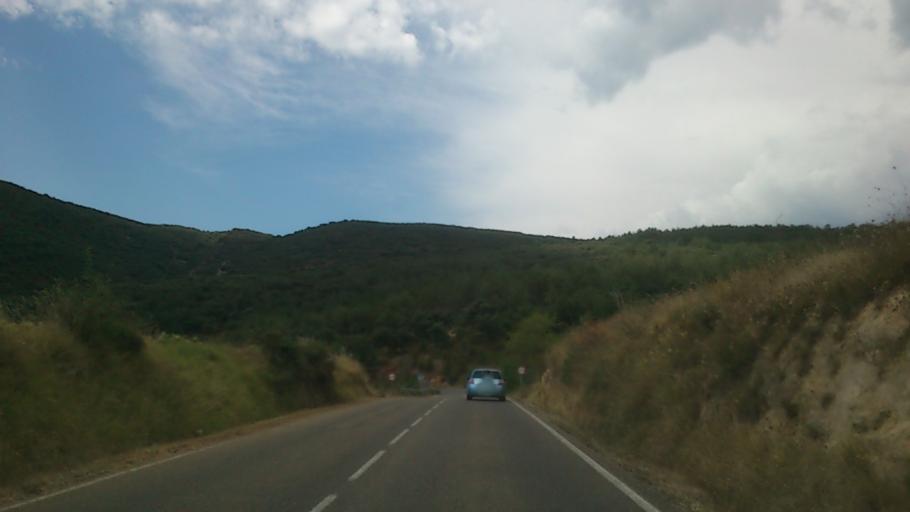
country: ES
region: Castille and Leon
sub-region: Provincia de Burgos
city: Frias
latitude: 42.7536
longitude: -3.2998
